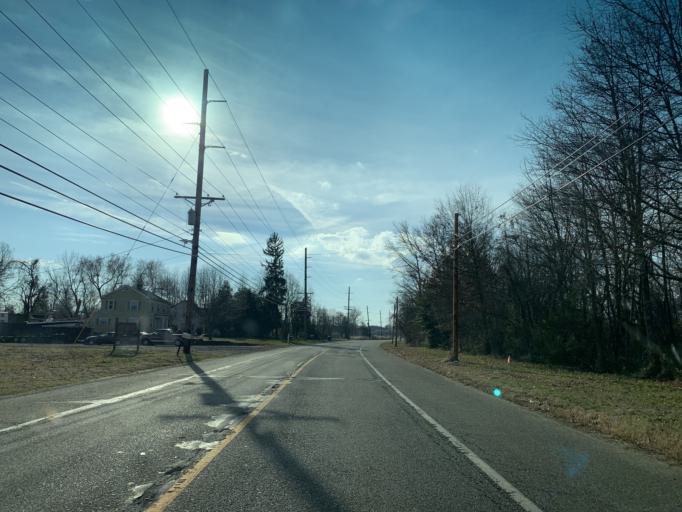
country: US
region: Delaware
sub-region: New Castle County
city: Claymont
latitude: 39.7644
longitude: -75.4297
